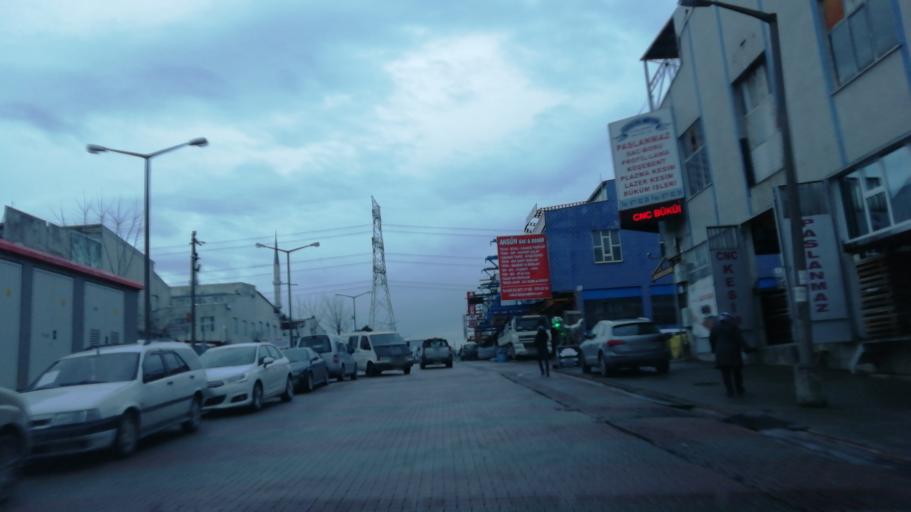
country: TR
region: Istanbul
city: Mahmutbey
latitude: 41.0671
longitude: 28.8064
